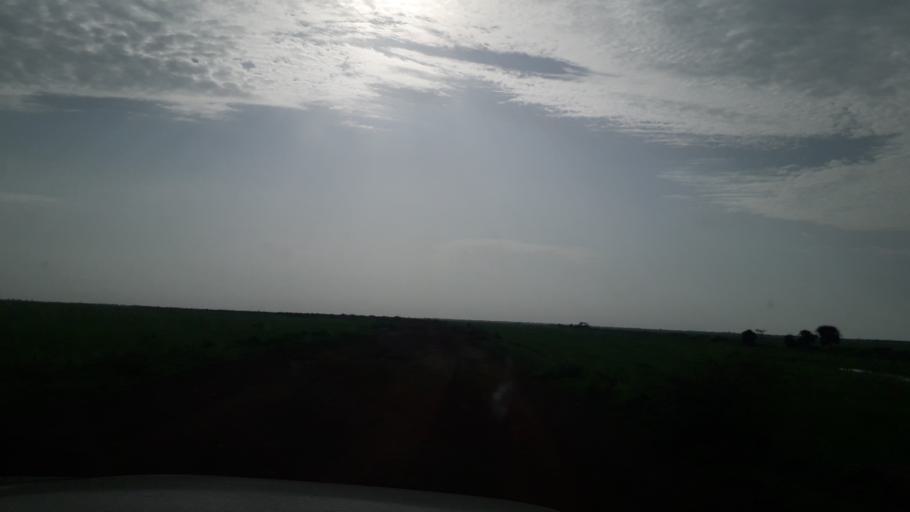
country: ET
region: Gambela
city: Gambela
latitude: 8.3610
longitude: 33.8574
